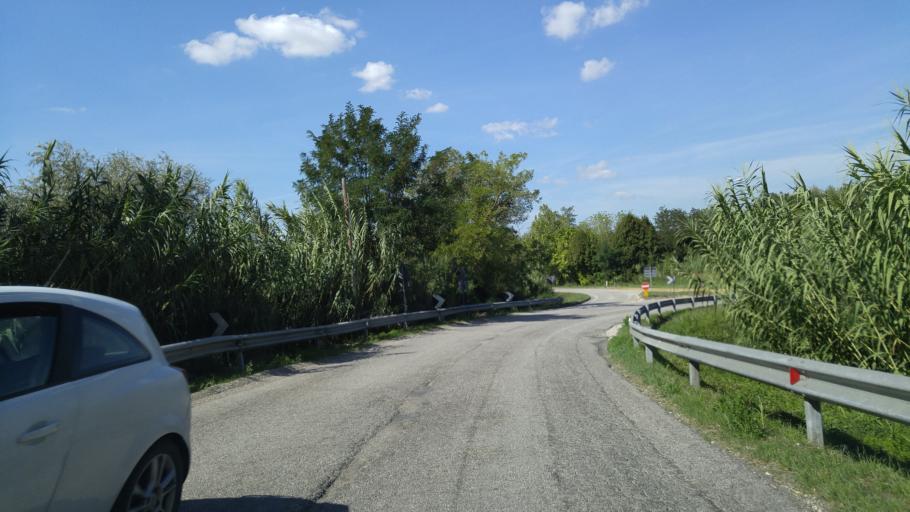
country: IT
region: The Marches
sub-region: Provincia di Pesaro e Urbino
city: Piagge
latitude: 43.7564
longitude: 12.9676
